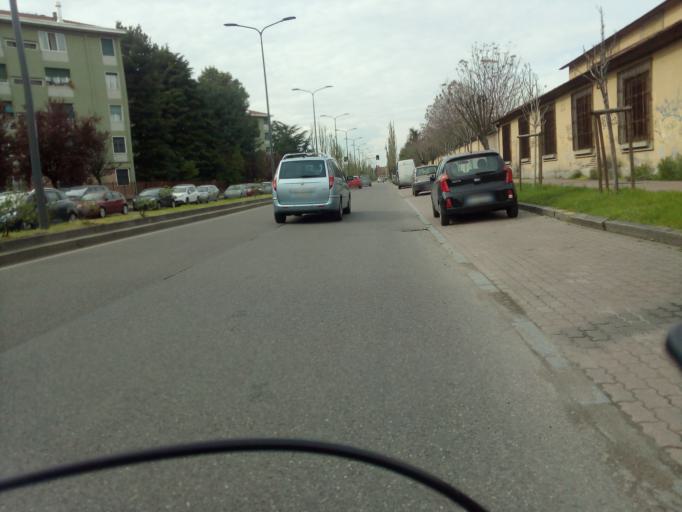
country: IT
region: Lombardy
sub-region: Citta metropolitana di Milano
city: Romano Banco
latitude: 45.4627
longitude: 9.1146
